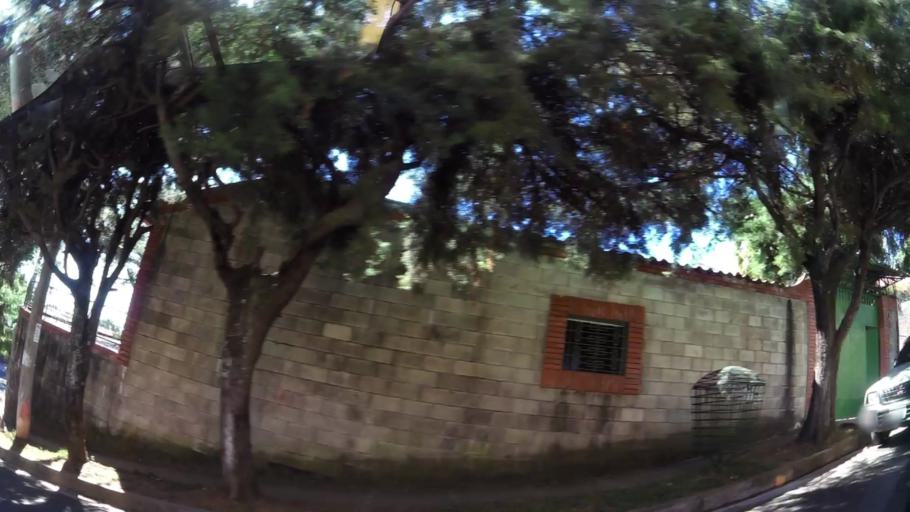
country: SV
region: Sonsonate
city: Juayua
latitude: 13.8454
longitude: -89.7433
